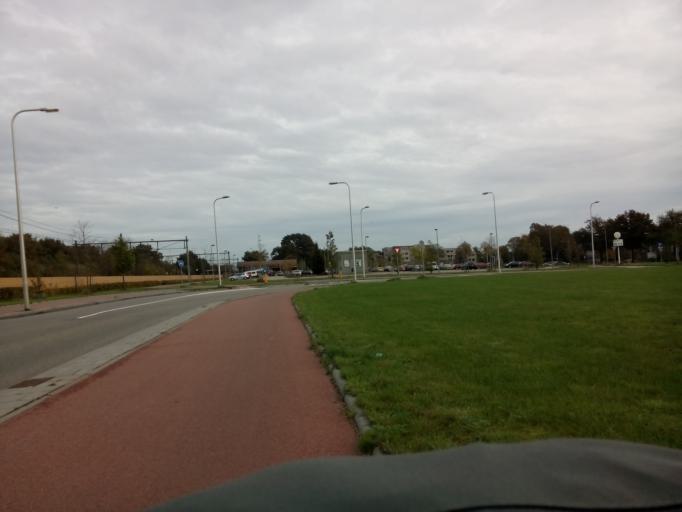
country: NL
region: Drenthe
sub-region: Gemeente Hoogeveen
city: Hoogeveen
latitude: 52.7316
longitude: 6.4700
